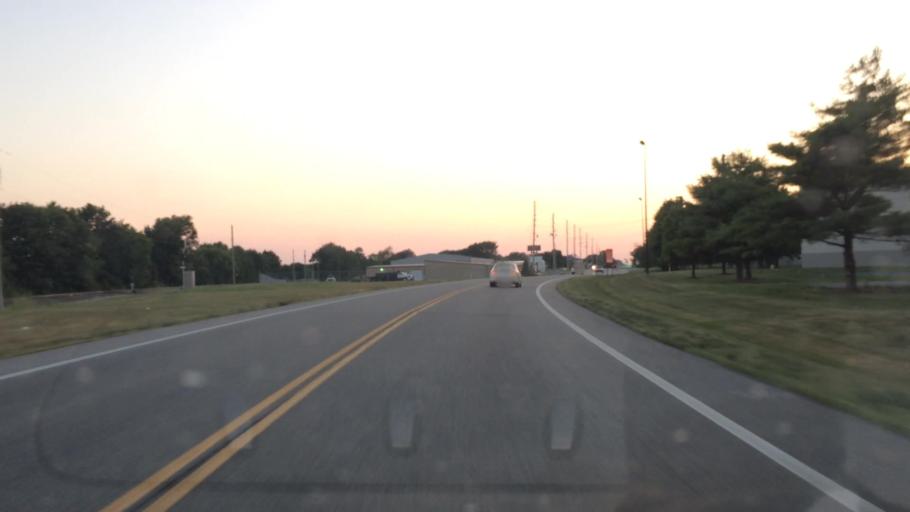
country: US
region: Missouri
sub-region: Greene County
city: Strafford
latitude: 37.2379
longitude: -93.2020
